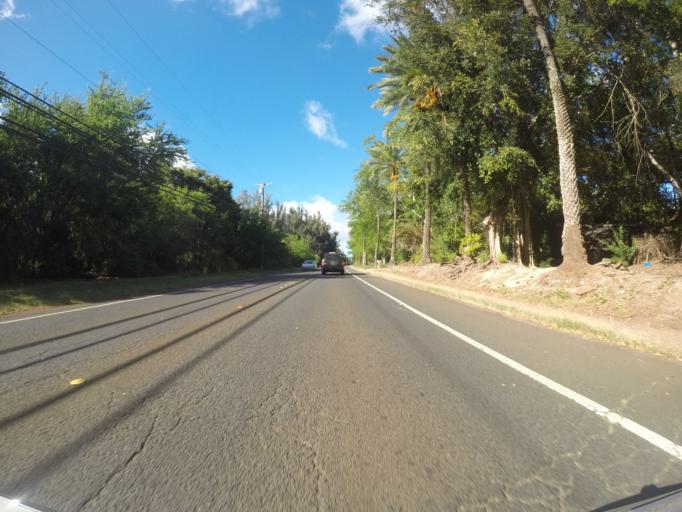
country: US
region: Hawaii
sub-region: Honolulu County
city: Hale'iwa
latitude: 21.6063
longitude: -158.0977
